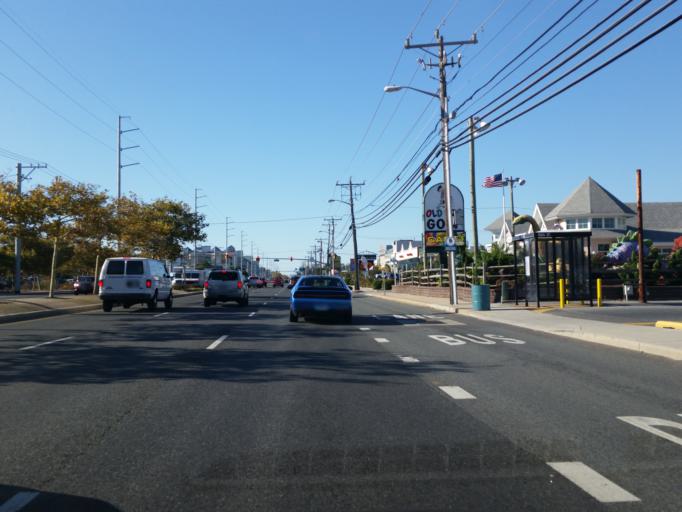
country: US
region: Maryland
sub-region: Worcester County
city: Ocean City
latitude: 38.3905
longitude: -75.0648
